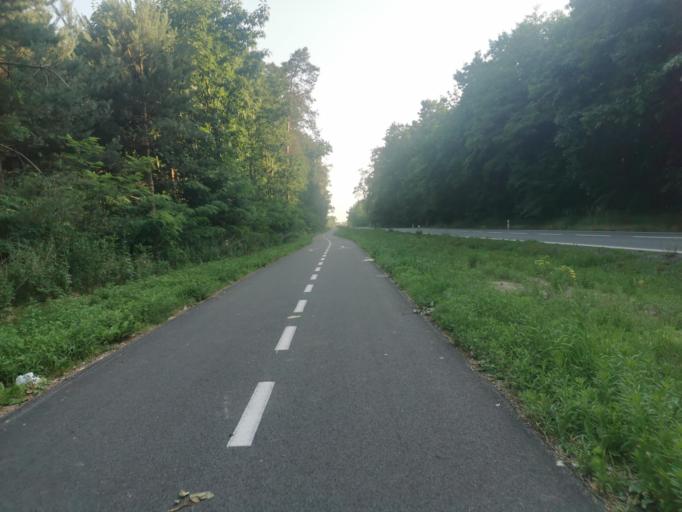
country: CZ
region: South Moravian
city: Ratiskovice
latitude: 48.8947
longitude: 17.1539
